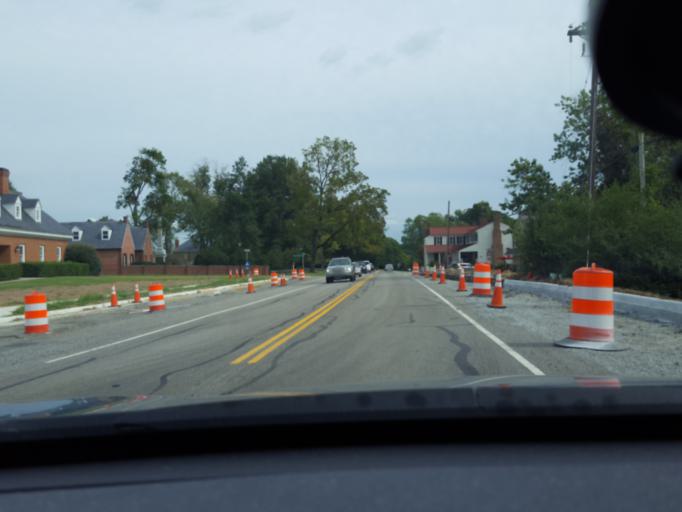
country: US
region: Virginia
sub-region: Hanover County
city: Hanover
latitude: 37.7637
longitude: -77.3685
